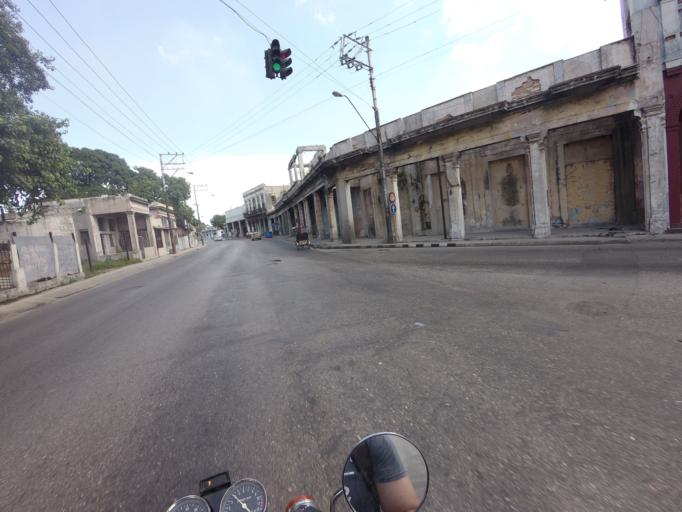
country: TM
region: Balkan
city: Gumdag
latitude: 38.8439
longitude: 54.1692
